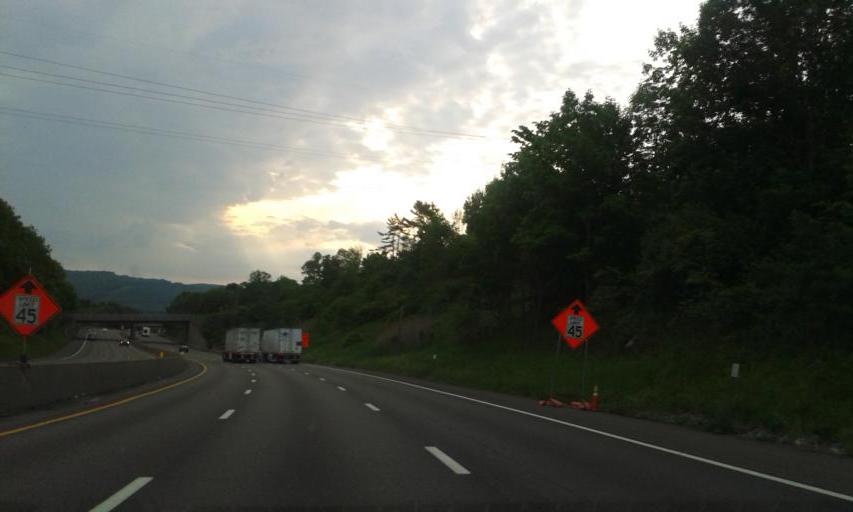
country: US
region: New York
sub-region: Broome County
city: Port Dickinson
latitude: 42.1120
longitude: -75.8732
